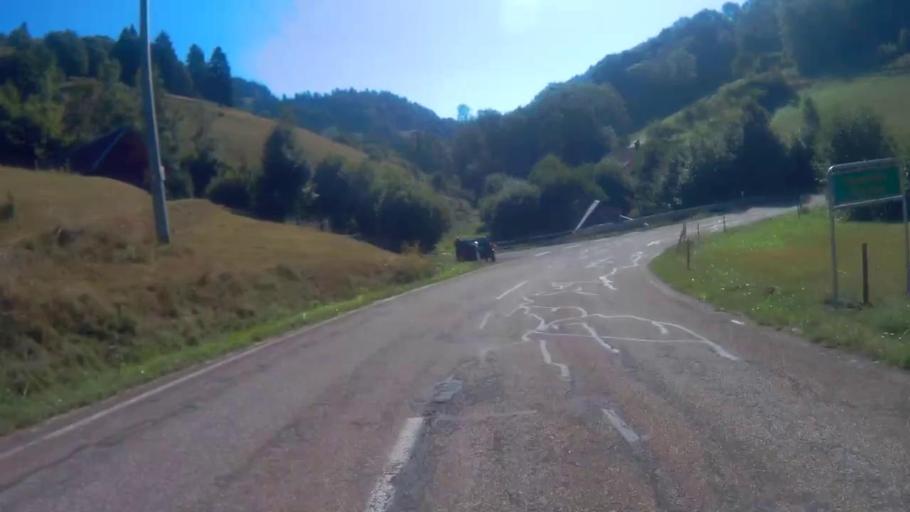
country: DE
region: Baden-Wuerttemberg
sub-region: Freiburg Region
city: Tunau
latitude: 47.7620
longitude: 7.9217
